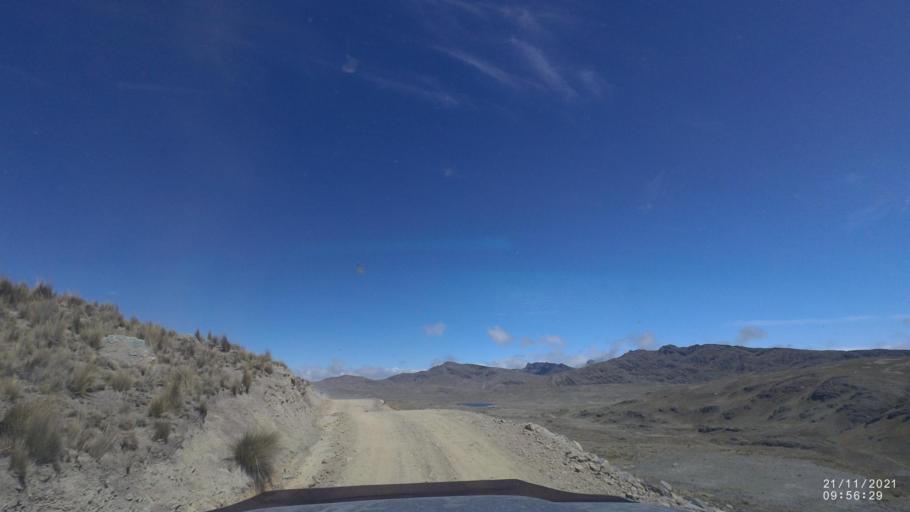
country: BO
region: Cochabamba
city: Cochabamba
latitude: -17.0414
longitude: -66.2662
